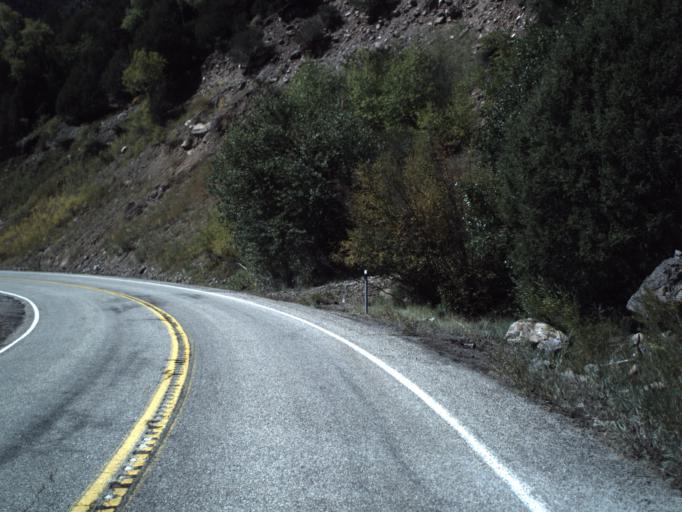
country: US
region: Utah
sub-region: Beaver County
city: Beaver
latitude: 38.2716
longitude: -112.4787
